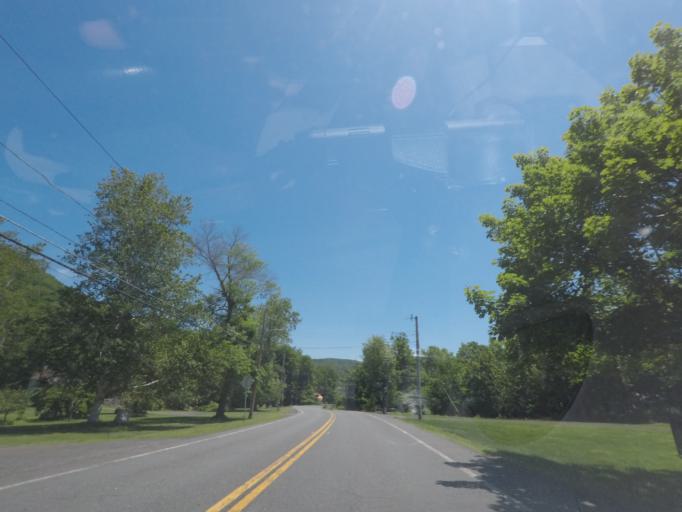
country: US
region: Massachusetts
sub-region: Berkshire County
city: Becket
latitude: 42.2678
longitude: -72.9655
